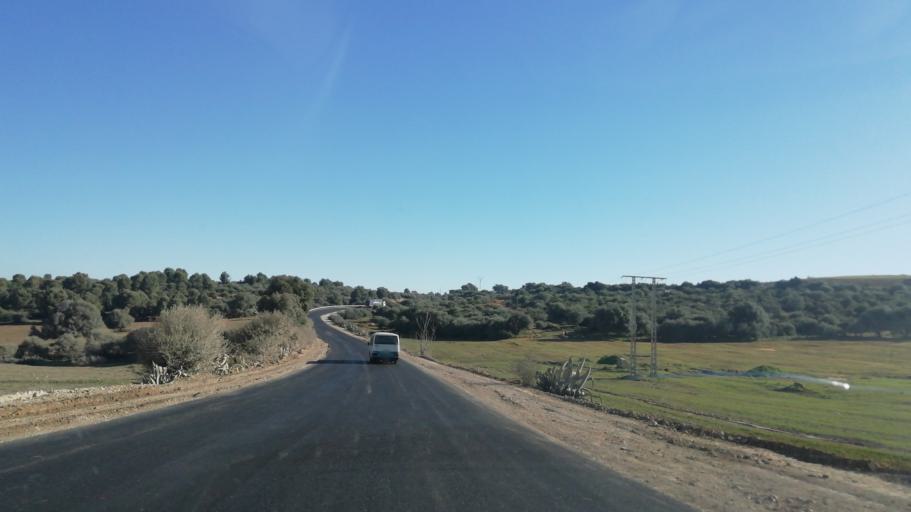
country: DZ
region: Relizane
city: Smala
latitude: 35.6684
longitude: 0.8079
